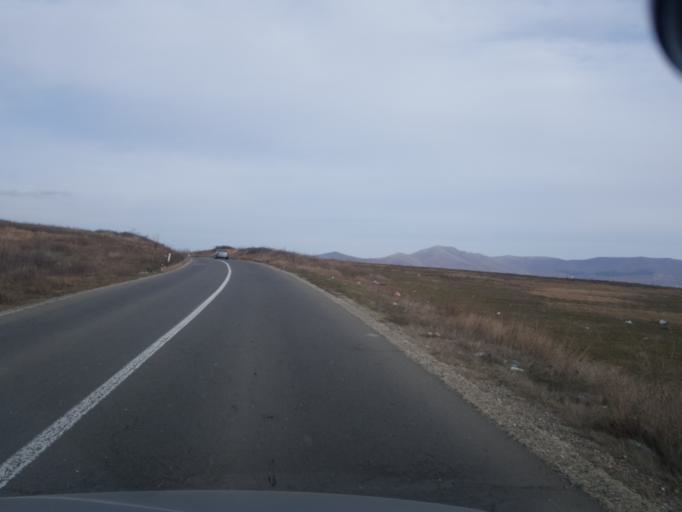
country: XK
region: Gjakova
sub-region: Komuna e Gjakoves
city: Gjakove
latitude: 42.4406
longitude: 20.4885
